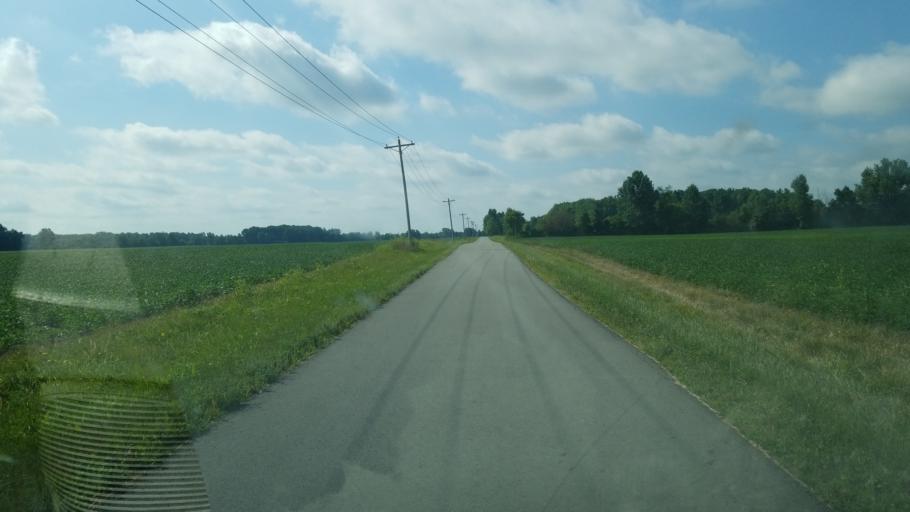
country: US
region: Ohio
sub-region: Wyandot County
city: Upper Sandusky
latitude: 40.7357
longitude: -83.3623
